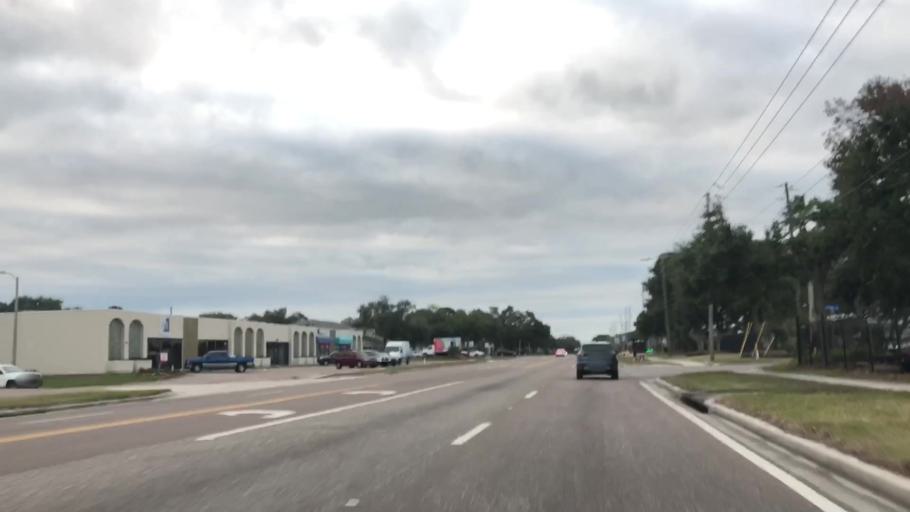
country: US
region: Florida
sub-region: Pinellas County
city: Dunedin
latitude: 27.9771
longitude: -82.7547
